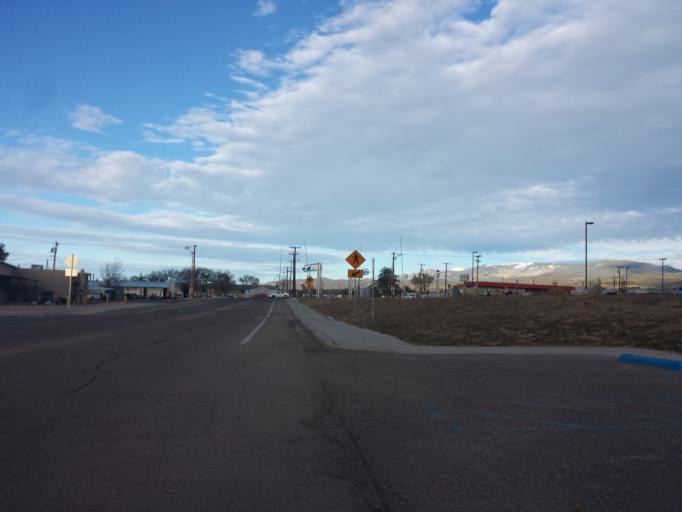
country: US
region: New Mexico
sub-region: Santa Fe County
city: Santa Fe
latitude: 35.6736
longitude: -105.9571
